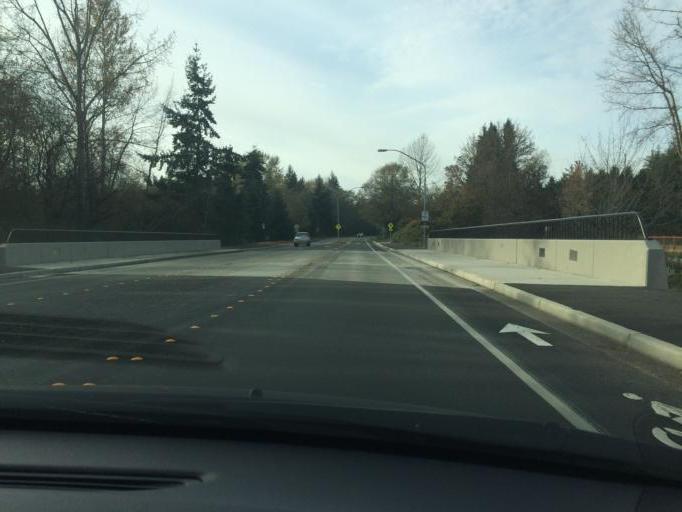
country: US
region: Washington
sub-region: Whatcom County
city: Bellingham
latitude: 48.7160
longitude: -122.4918
